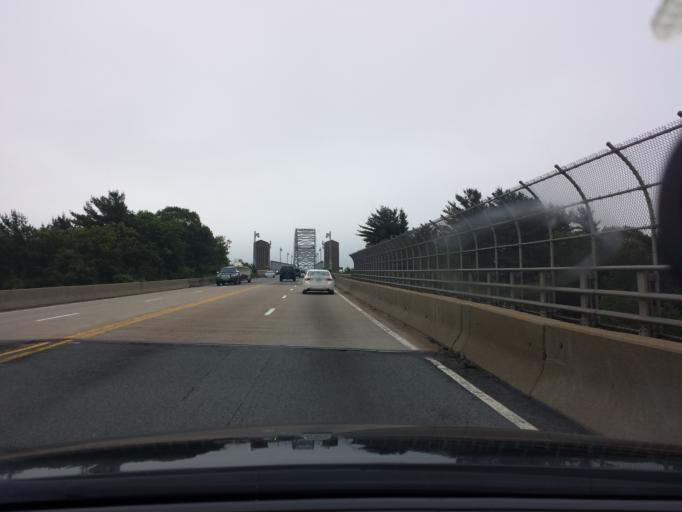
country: US
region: Massachusetts
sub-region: Barnstable County
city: Bourne
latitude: 41.7520
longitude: -70.5924
